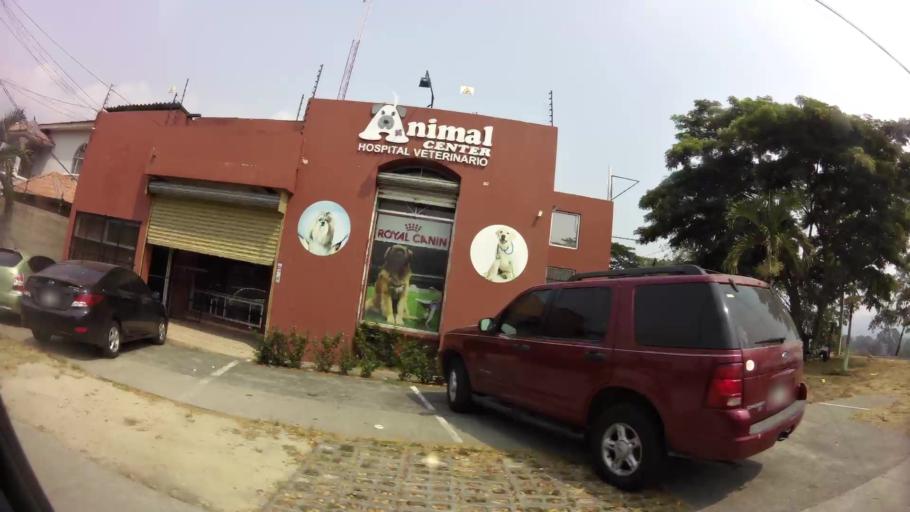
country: HN
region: Cortes
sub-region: San Pedro Sula
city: Pena Blanca
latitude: 15.5585
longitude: -88.0173
